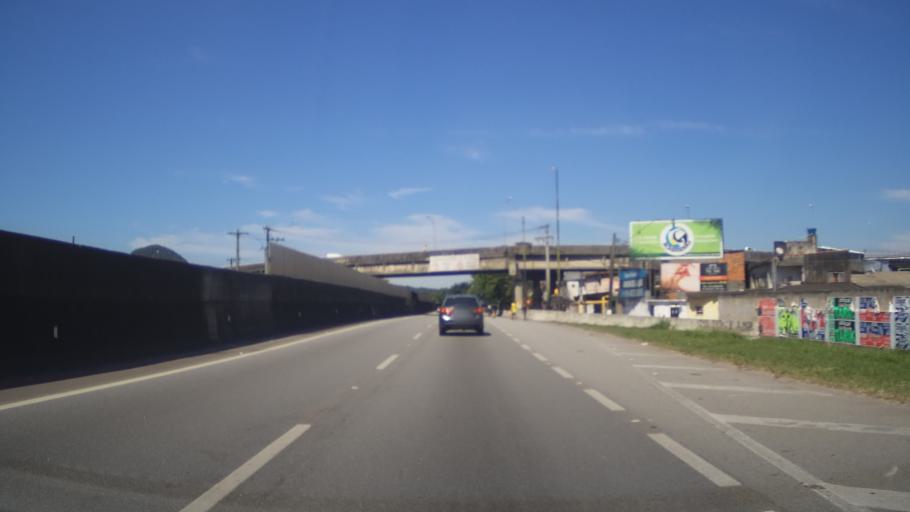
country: BR
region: Sao Paulo
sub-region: Sao Vicente
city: Sao Vicente
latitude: -23.9678
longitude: -46.4007
